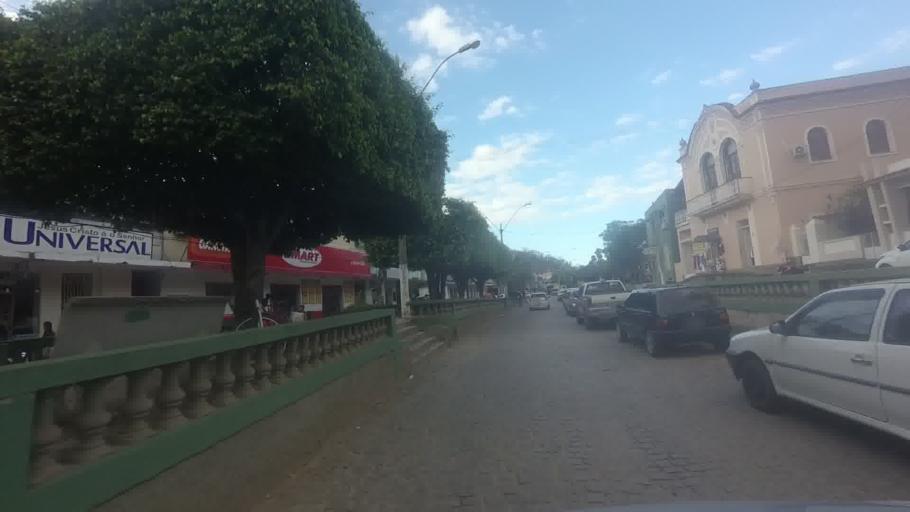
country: BR
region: Espirito Santo
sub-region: Mimoso Do Sul
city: Mimoso do Sul
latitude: -20.9529
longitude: -41.3475
